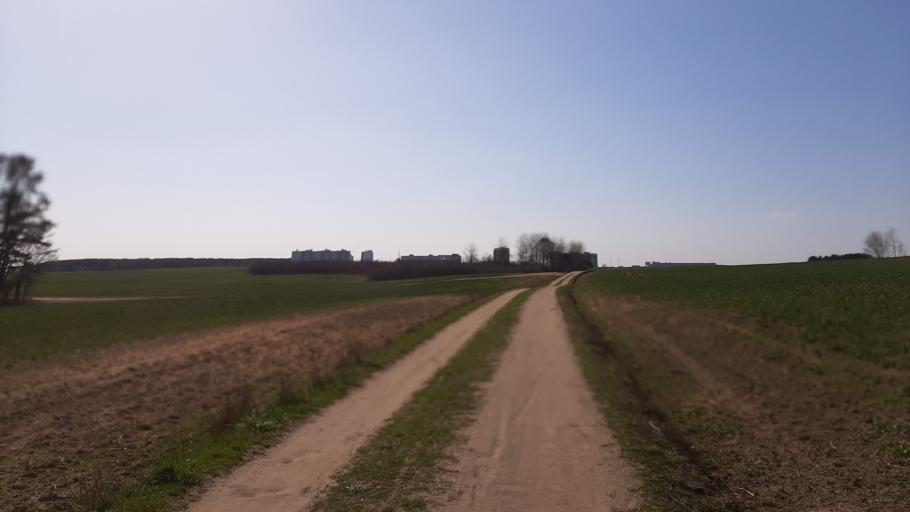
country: BY
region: Minsk
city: Bal'shavik
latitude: 53.9591
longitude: 27.5685
